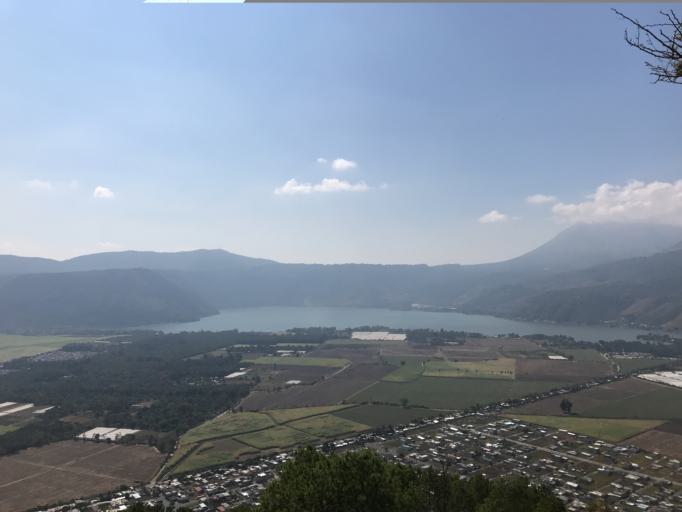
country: GT
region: Guatemala
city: Villa Canales
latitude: 14.4772
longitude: -90.5466
